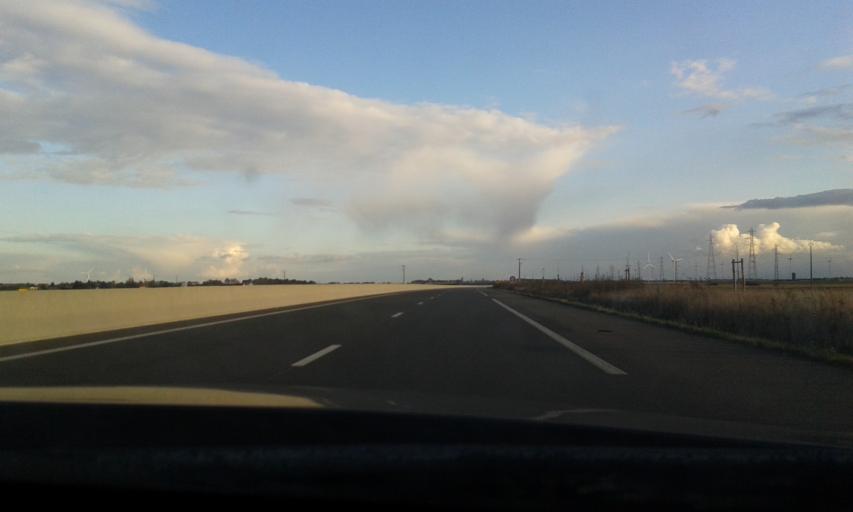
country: FR
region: Centre
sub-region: Departement d'Eure-et-Loir
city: Sours
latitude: 48.3554
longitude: 1.6142
